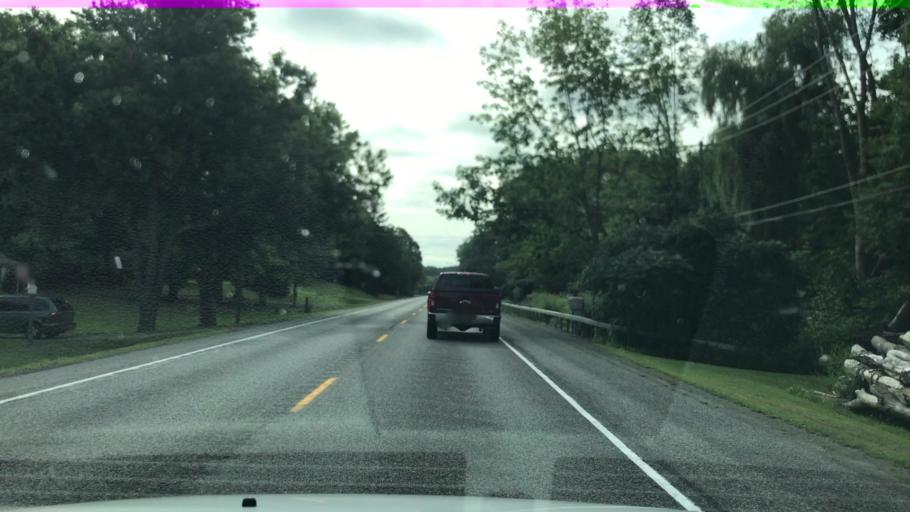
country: US
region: New York
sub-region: Erie County
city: Alden
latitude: 42.8484
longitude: -78.4810
